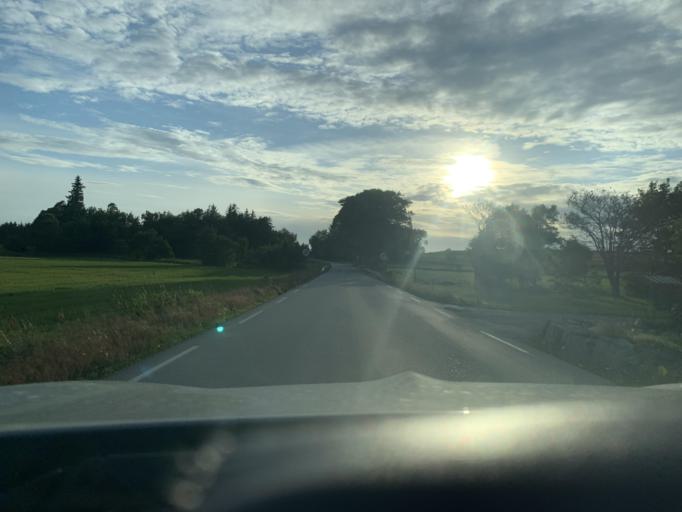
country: NO
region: Rogaland
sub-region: Ha
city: Naerbo
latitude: 58.6847
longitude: 5.7437
